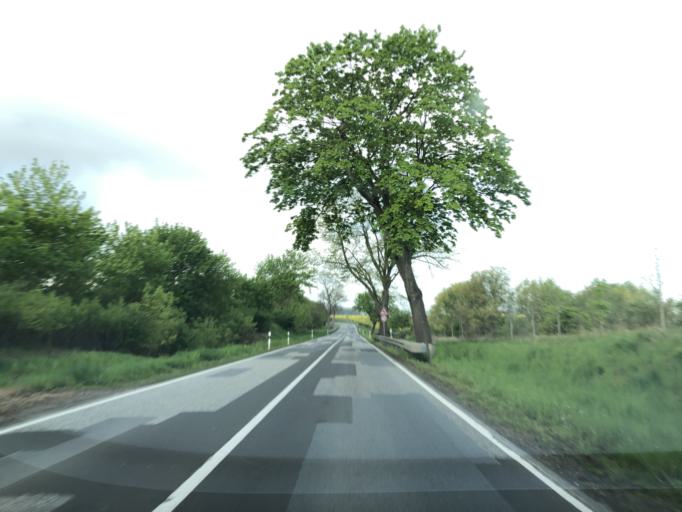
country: DE
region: Mecklenburg-Vorpommern
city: Guestrow
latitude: 53.7687
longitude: 12.1536
